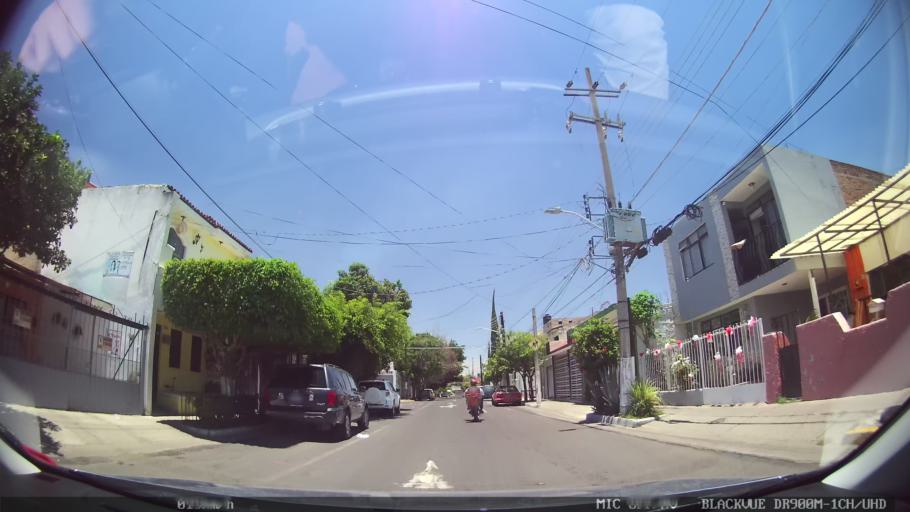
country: MX
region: Jalisco
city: Tlaquepaque
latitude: 20.6765
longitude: -103.2825
